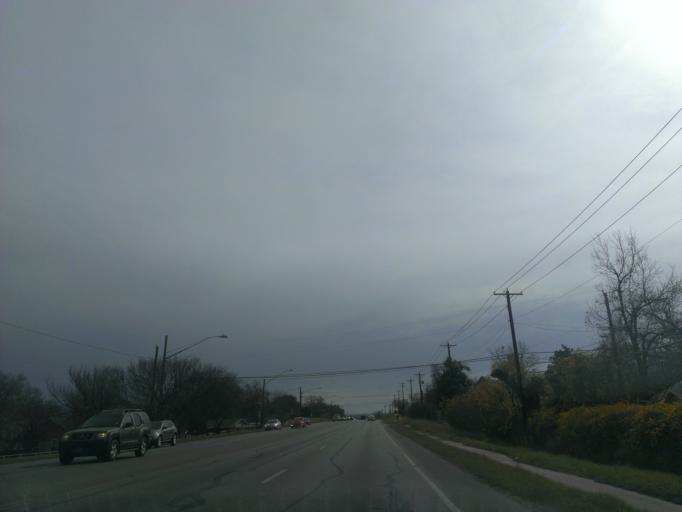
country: US
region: Texas
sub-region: Travis County
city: Austin
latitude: 30.2805
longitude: -97.7028
